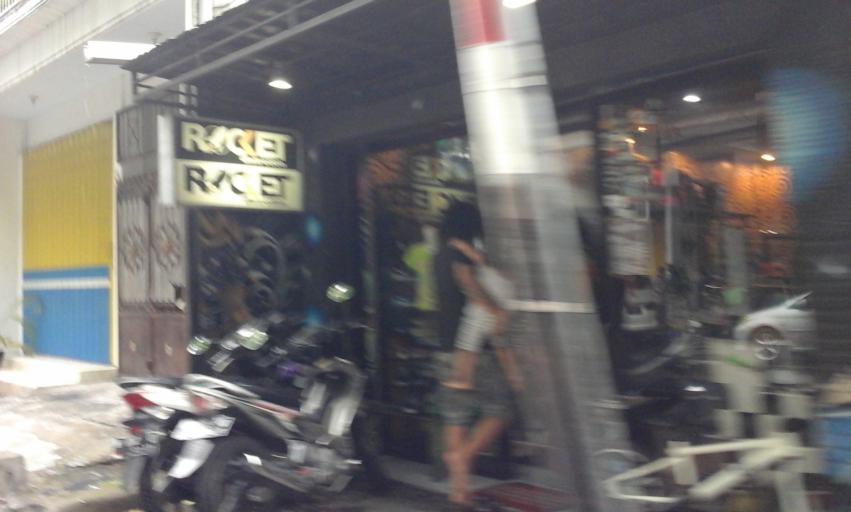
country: ID
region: East Java
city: Lumajang
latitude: -8.1329
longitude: 113.2215
